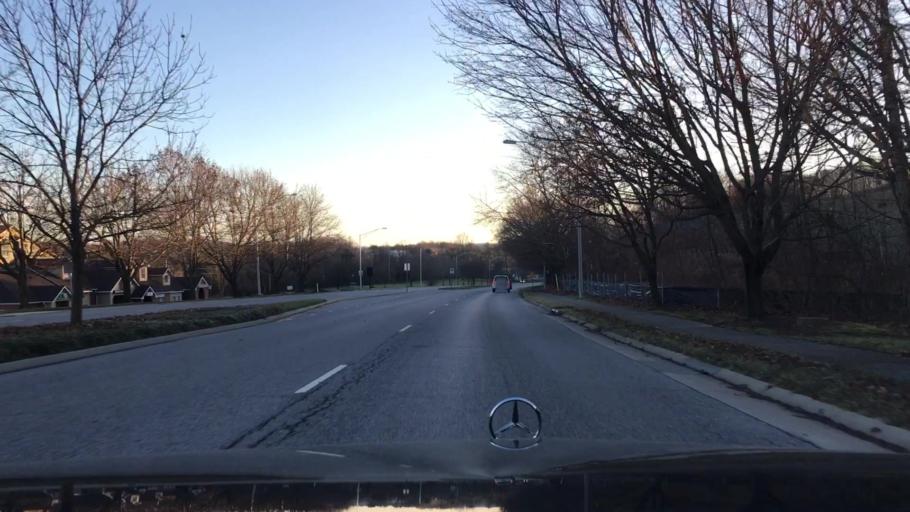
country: US
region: Virginia
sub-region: Montgomery County
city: Blacksburg
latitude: 37.2062
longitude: -80.3990
